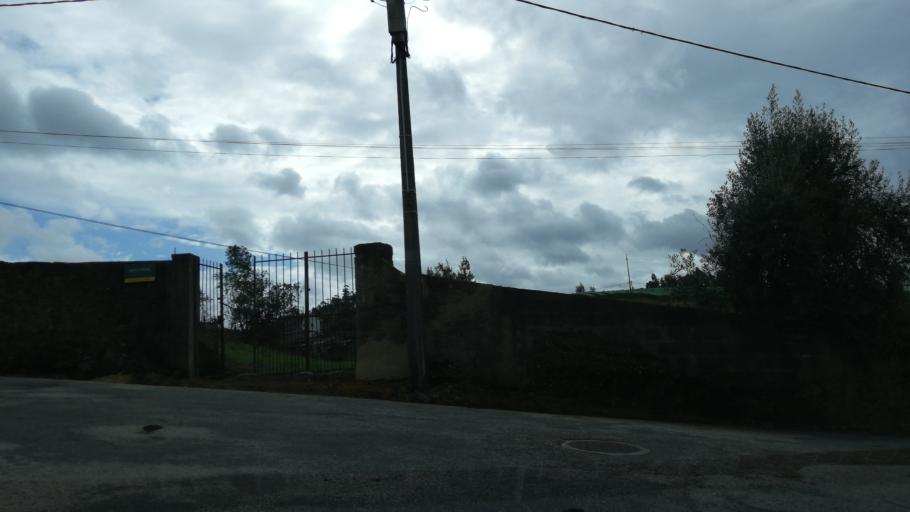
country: PT
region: Aveiro
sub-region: Agueda
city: Valongo
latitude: 40.6194
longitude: -8.4234
